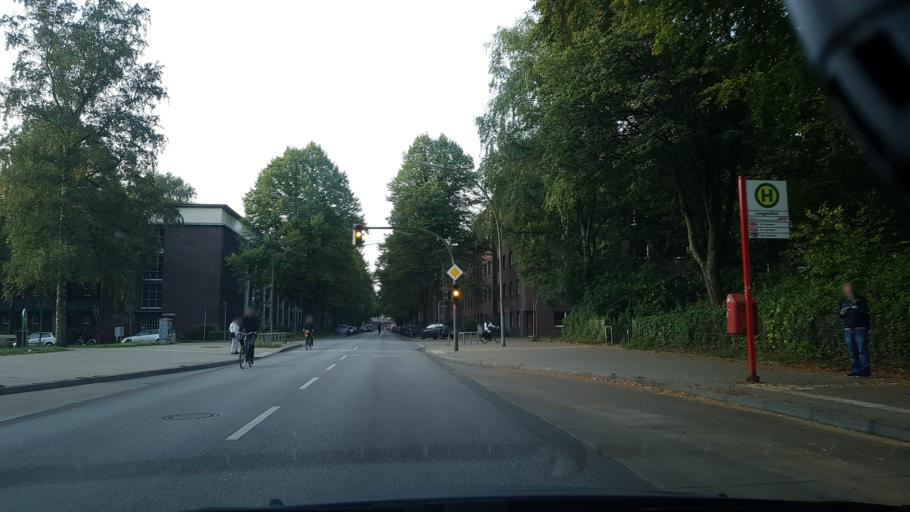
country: DE
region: Hamburg
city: Barmbek-Nord
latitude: 53.5999
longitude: 10.0507
